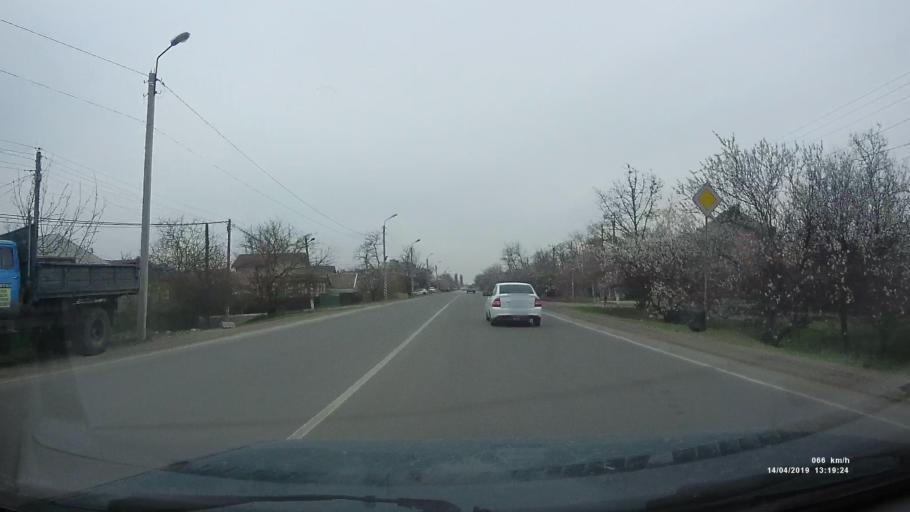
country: RU
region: Rostov
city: Kuleshovka
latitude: 47.0806
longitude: 39.5456
